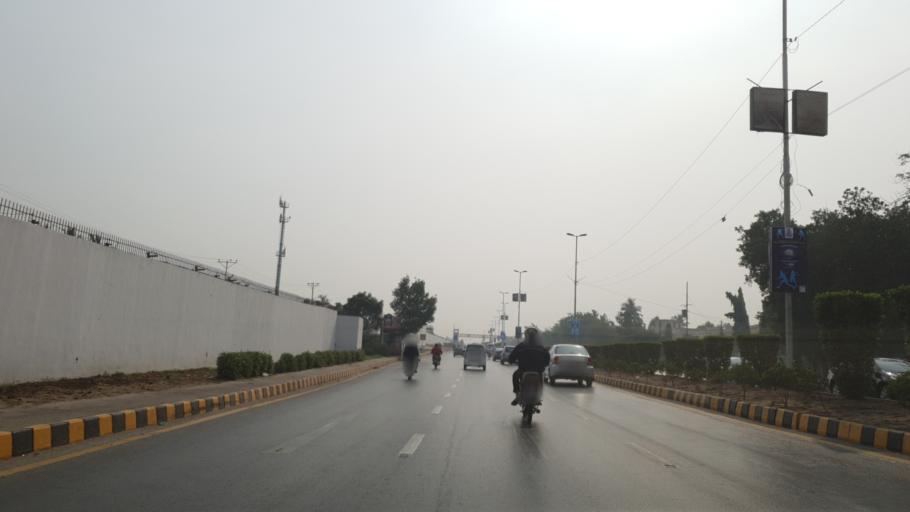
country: PK
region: Sindh
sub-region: Karachi District
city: Karachi
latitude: 24.8837
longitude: 67.0905
